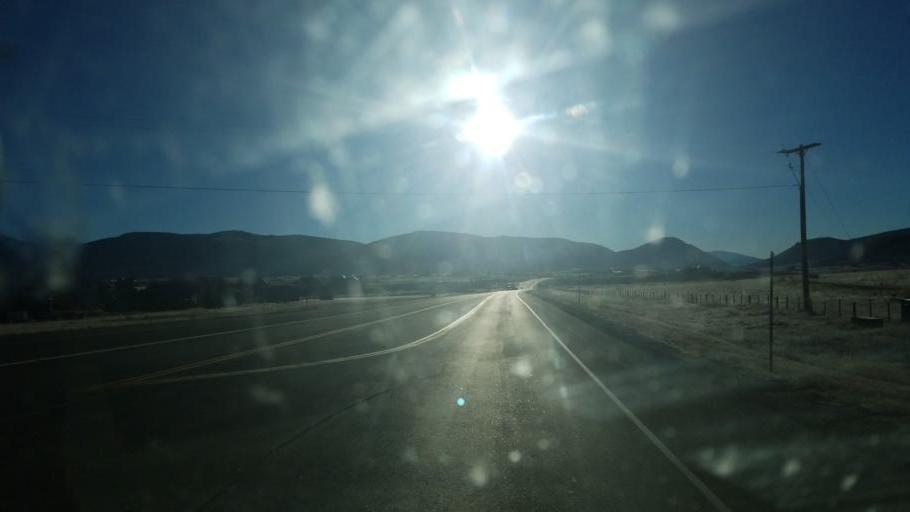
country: US
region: Colorado
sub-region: Gunnison County
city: Crested Butte
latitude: 38.8551
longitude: -106.9602
